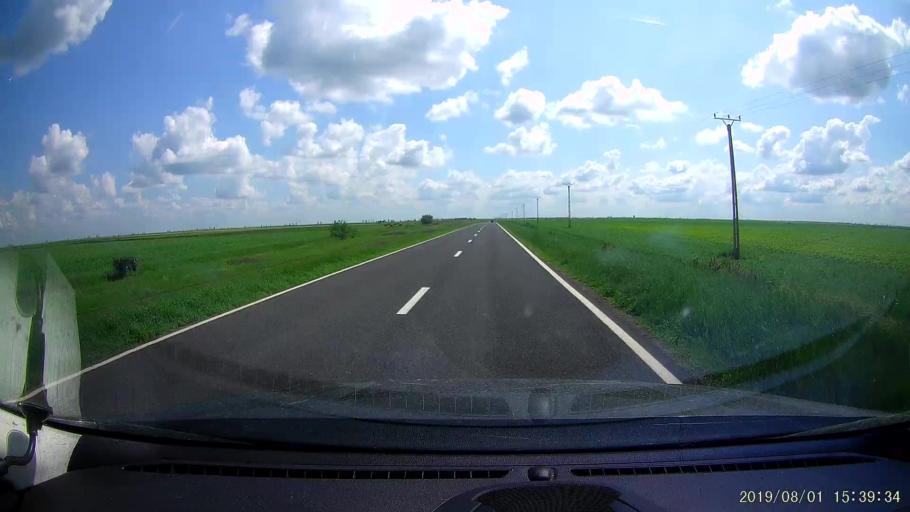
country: RO
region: Braila
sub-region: Comuna Baraganul
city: Baraganul
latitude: 44.8547
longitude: 27.5571
